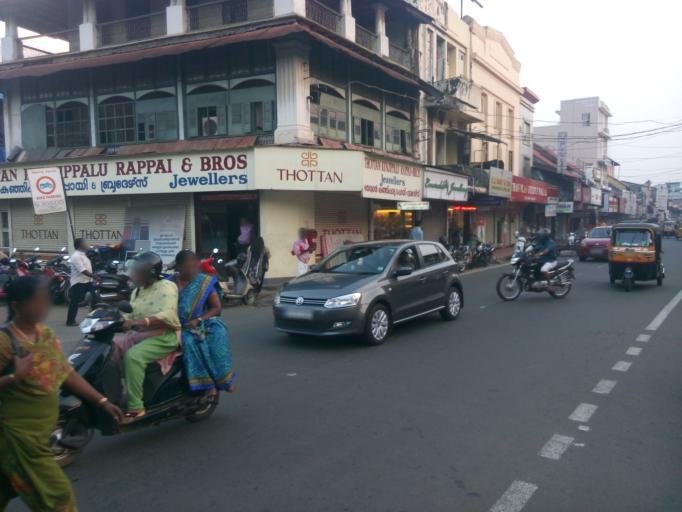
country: IN
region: Kerala
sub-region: Thrissur District
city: Trichur
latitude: 10.5219
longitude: 76.2168
